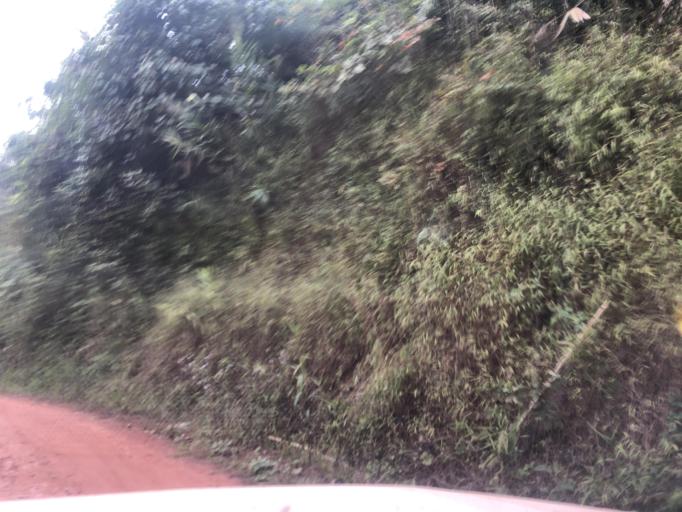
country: CN
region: Yunnan
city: Menglie
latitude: 22.1190
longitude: 101.7335
